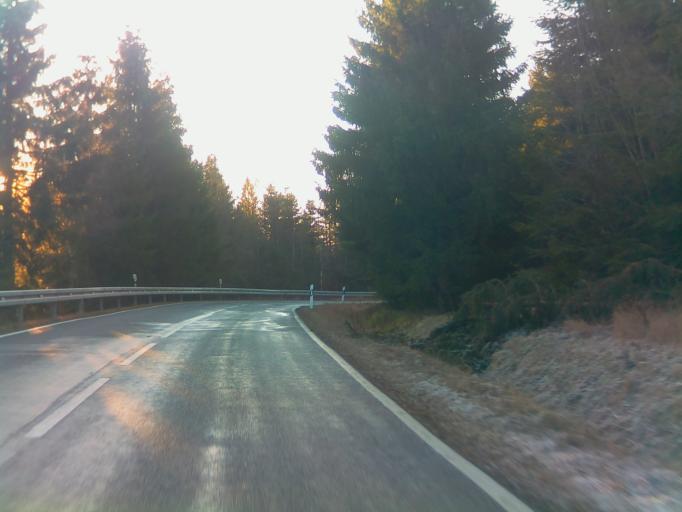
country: DE
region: Bavaria
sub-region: Upper Franconia
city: Tettau
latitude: 50.4579
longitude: 11.2529
